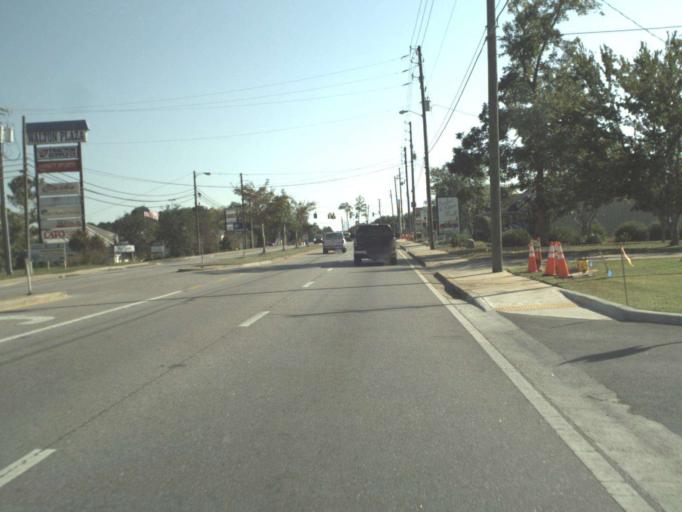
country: US
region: Florida
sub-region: Walton County
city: DeFuniak Springs
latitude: 30.7095
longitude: -86.1229
